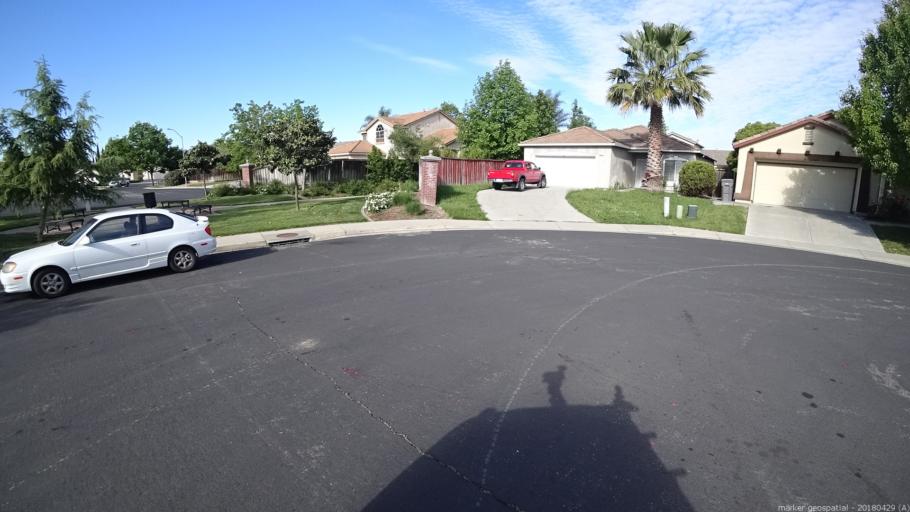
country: US
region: California
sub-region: Yolo County
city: West Sacramento
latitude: 38.5397
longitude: -121.5635
